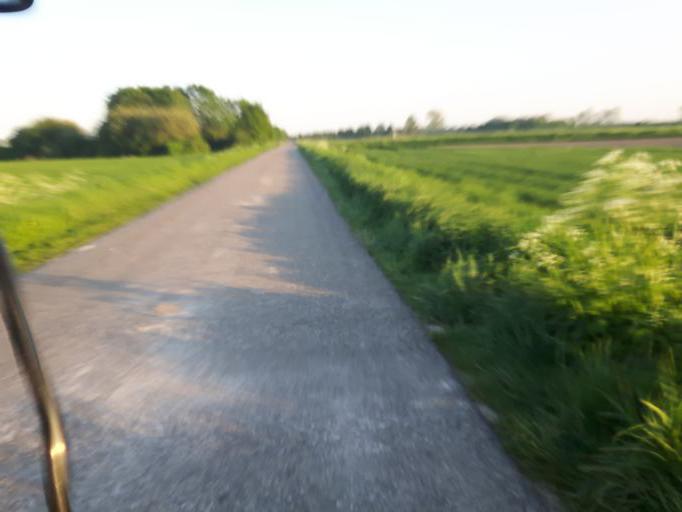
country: NL
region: Zeeland
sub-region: Gemeente Goes
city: Goes
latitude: 51.5062
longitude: 3.8090
